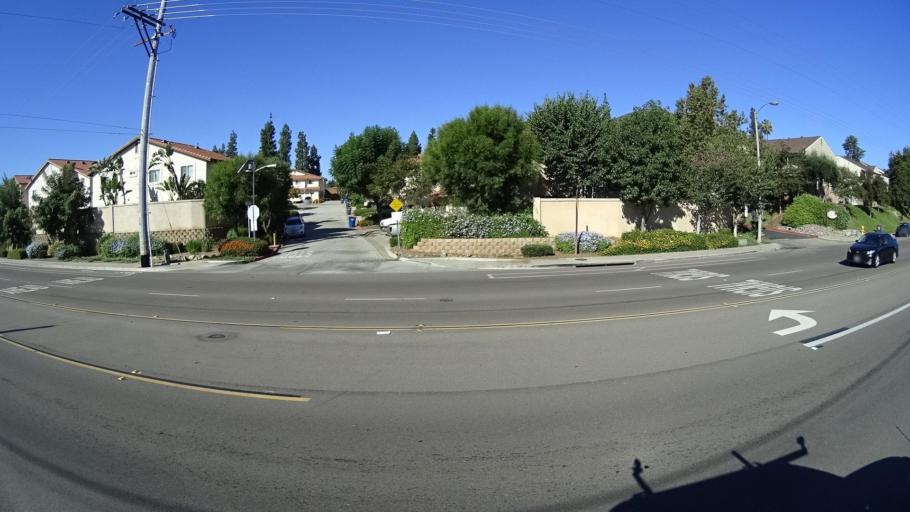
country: US
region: California
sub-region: San Diego County
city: Winter Gardens
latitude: 32.8222
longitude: -116.9334
